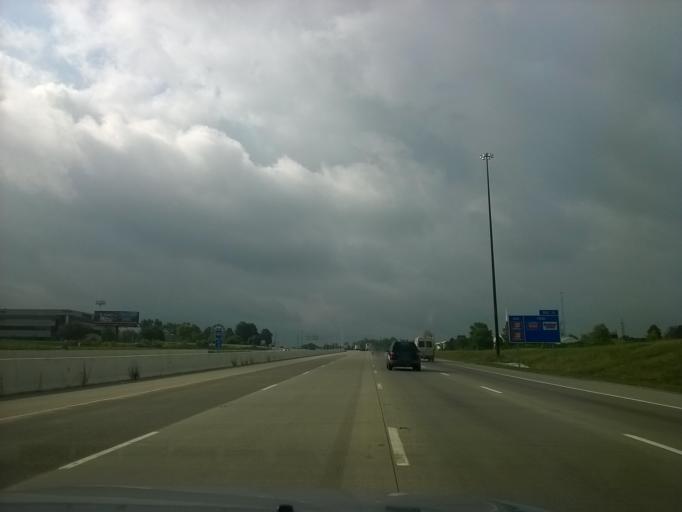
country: US
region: Indiana
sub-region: Marion County
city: Speedway
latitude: 39.7789
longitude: -86.2705
